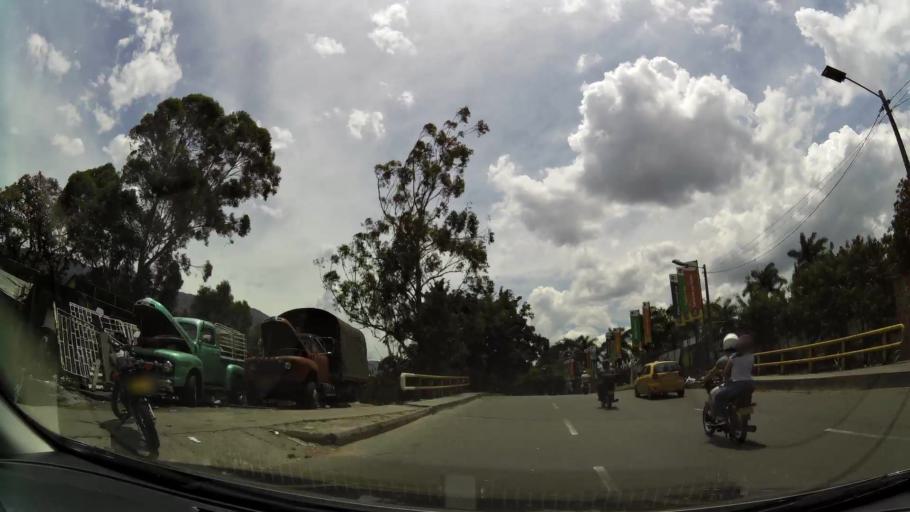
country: CO
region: Antioquia
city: Bello
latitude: 6.3314
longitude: -75.5597
